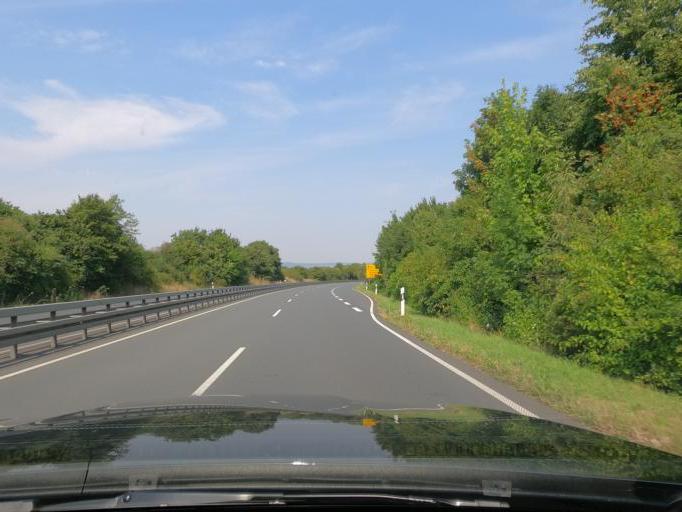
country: DE
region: Lower Saxony
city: Wennigsen
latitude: 52.2432
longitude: 9.6335
